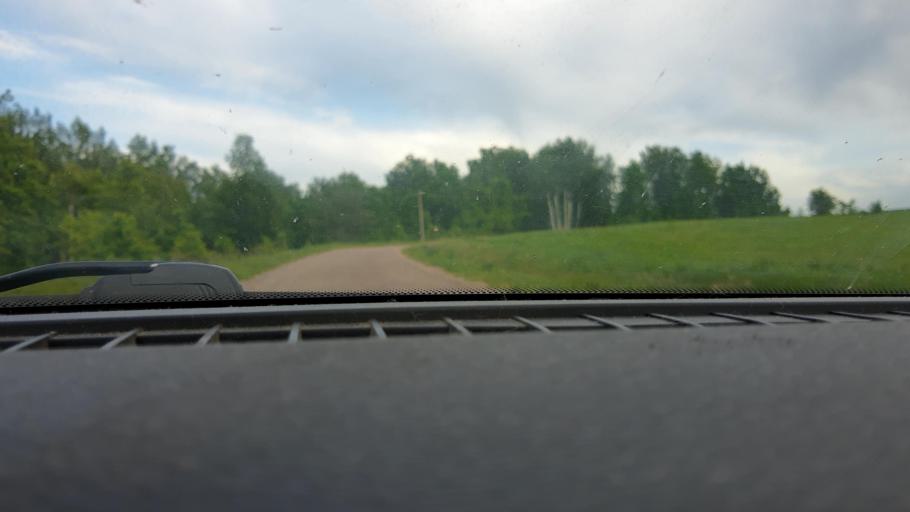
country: RU
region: Bashkortostan
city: Avdon
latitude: 54.4280
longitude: 55.8412
